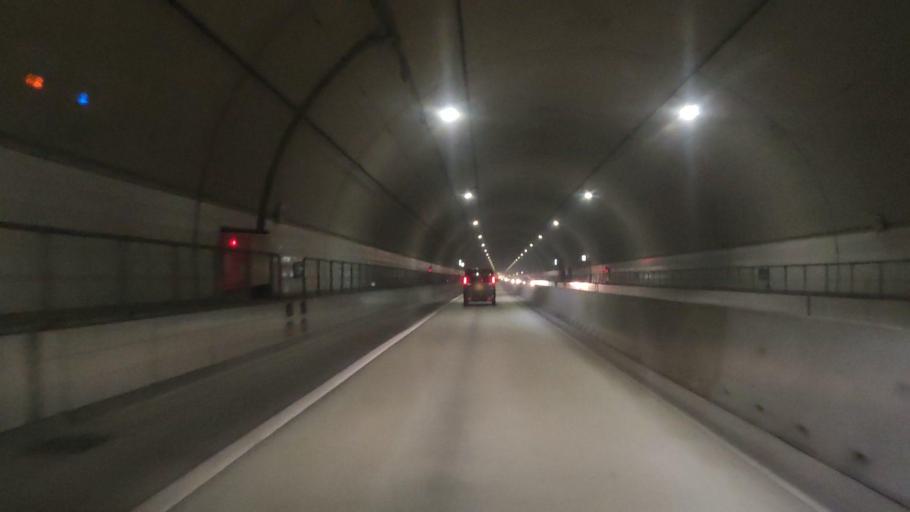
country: JP
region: Kumamoto
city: Ozu
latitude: 32.9035
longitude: 130.9496
